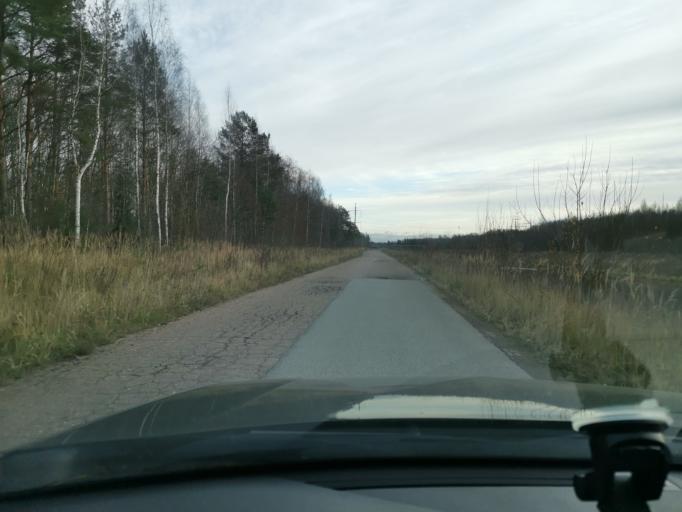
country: EE
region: Ida-Virumaa
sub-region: Sillamaee linn
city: Sillamae
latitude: 59.2652
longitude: 27.8996
